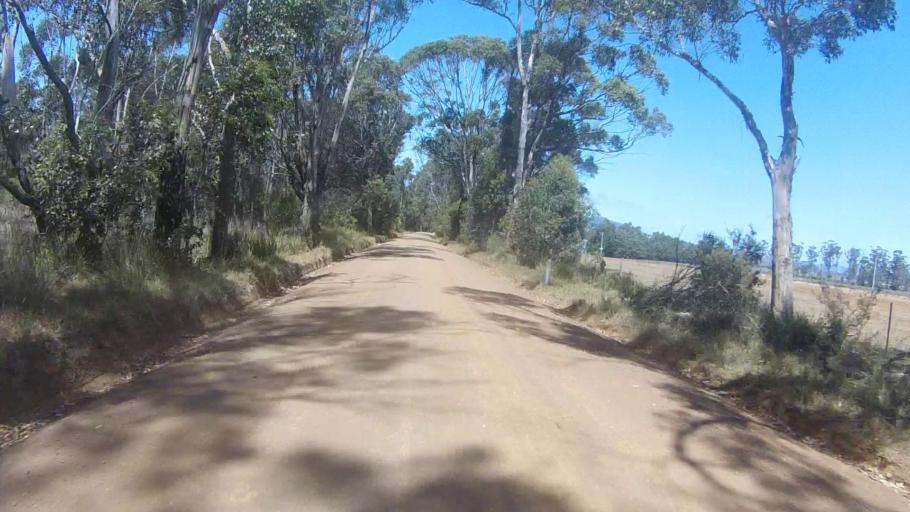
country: AU
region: Tasmania
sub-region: Sorell
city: Sorell
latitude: -42.8537
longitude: 147.8316
